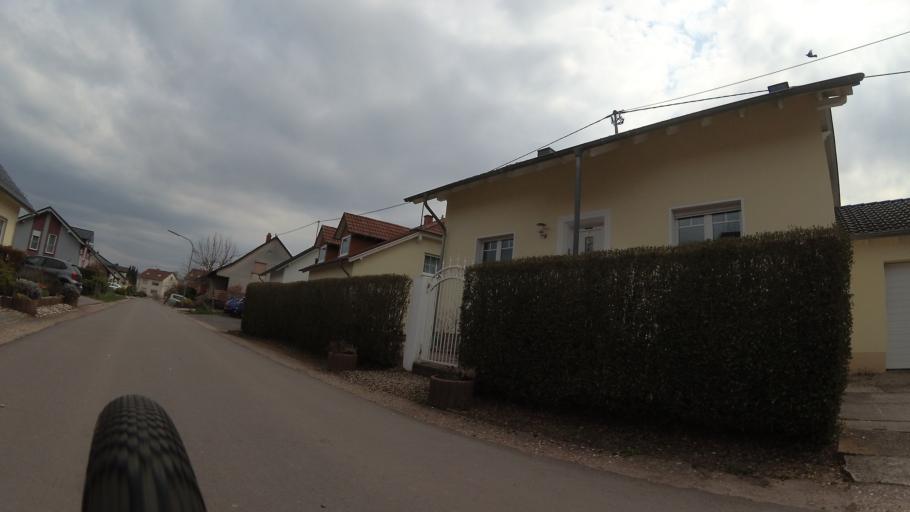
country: DE
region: Saarland
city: Merzig
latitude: 49.4408
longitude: 6.6063
